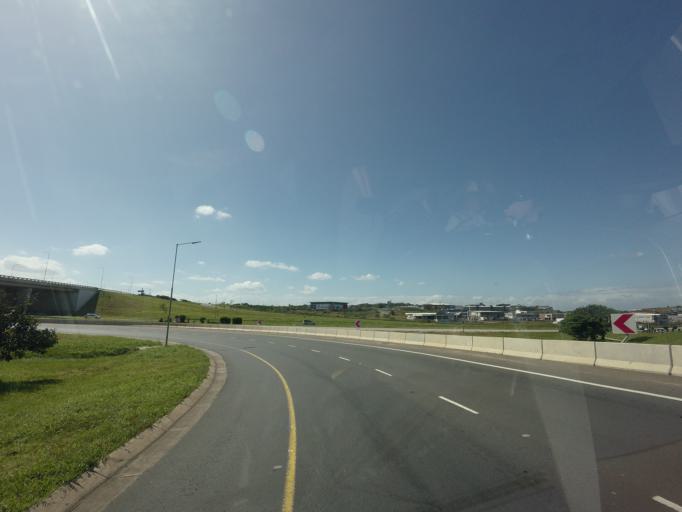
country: ZA
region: KwaZulu-Natal
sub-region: iLembe District Municipality
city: Ballitoville
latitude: -29.5173
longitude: 31.1987
